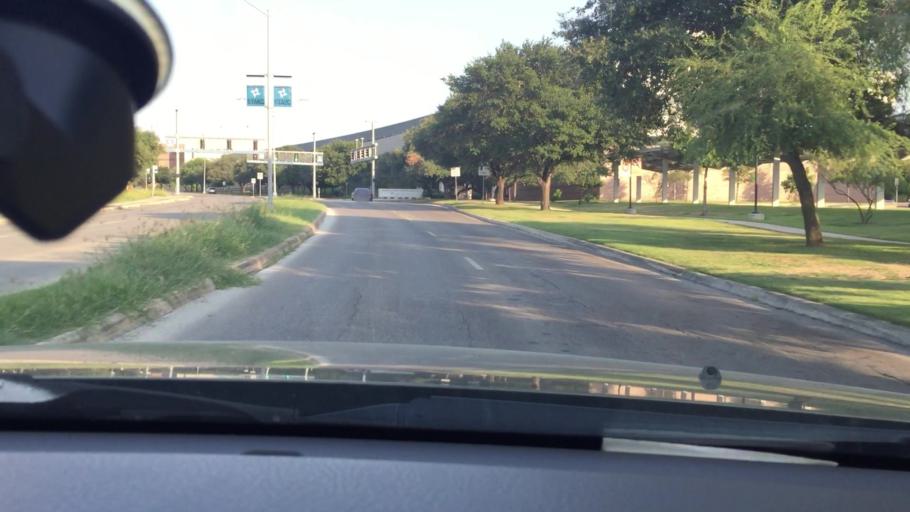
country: US
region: Texas
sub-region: Bexar County
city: Leon Valley
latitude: 29.5155
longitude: -98.5844
